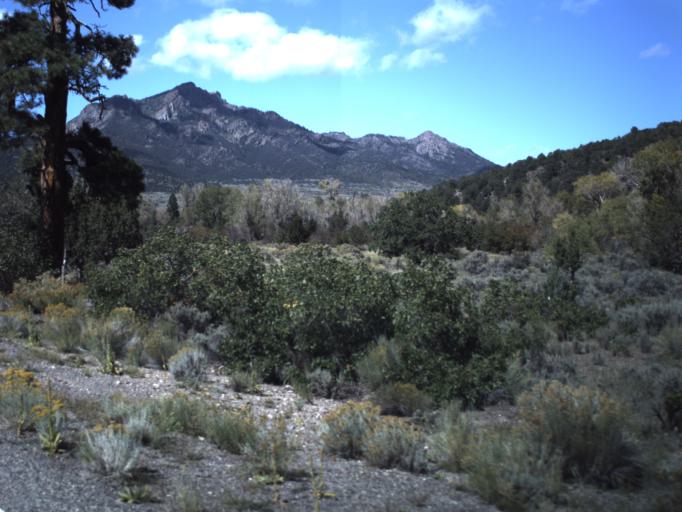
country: US
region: Utah
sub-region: Piute County
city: Junction
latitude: 38.2600
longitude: -112.2918
